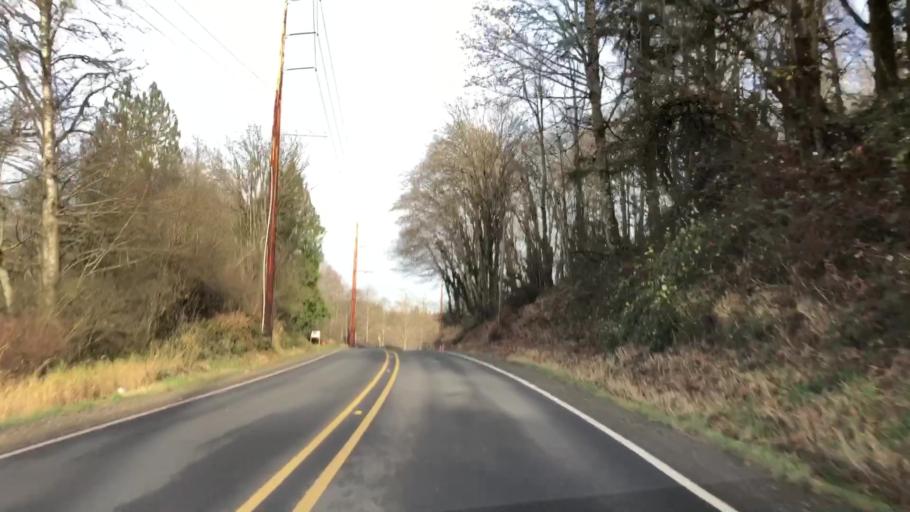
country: US
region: Washington
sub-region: Kitsap County
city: Indianola
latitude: 47.7774
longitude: -122.5550
